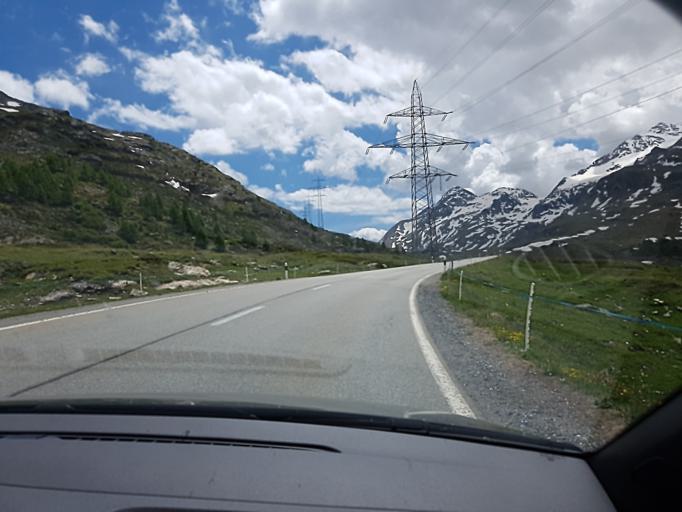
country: CH
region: Grisons
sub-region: Maloja District
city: Pontresina
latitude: 46.4343
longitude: 9.9966
